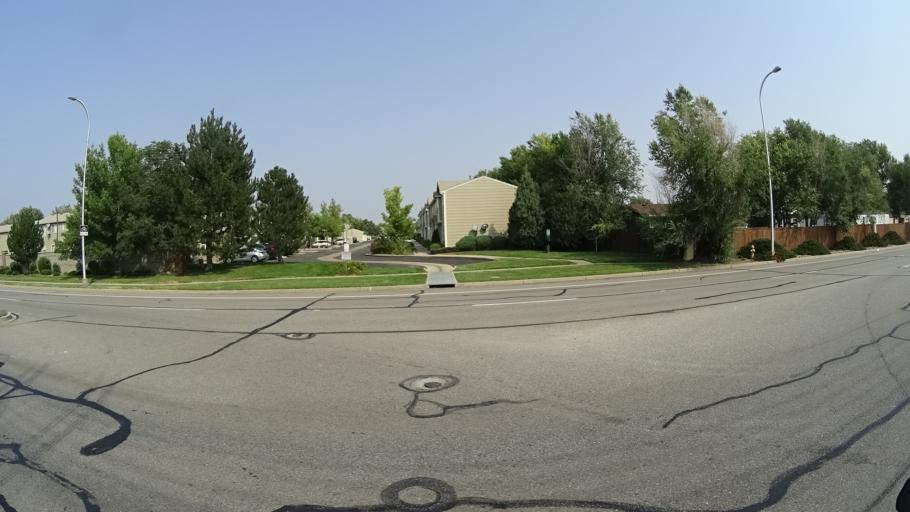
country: US
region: Colorado
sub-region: El Paso County
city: Cimarron Hills
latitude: 38.8251
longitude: -104.7343
